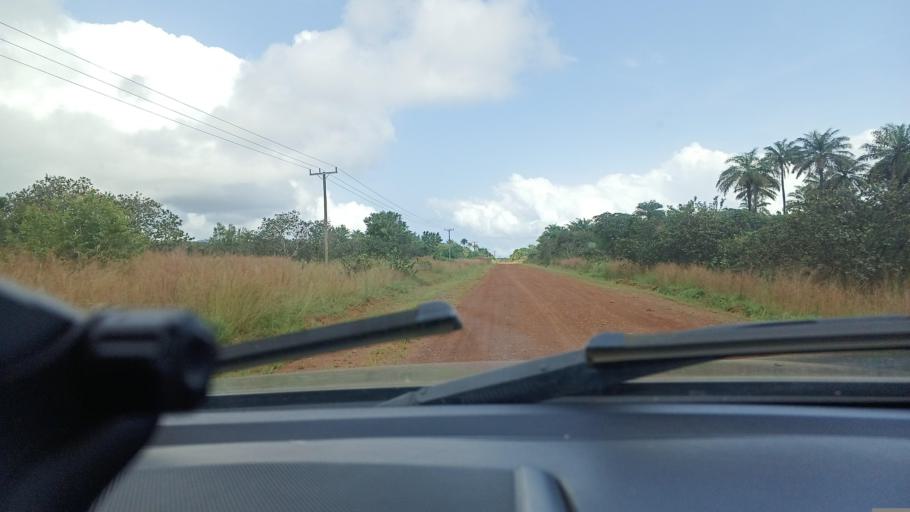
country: LR
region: Grand Cape Mount
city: Robertsport
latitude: 6.6948
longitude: -11.2835
